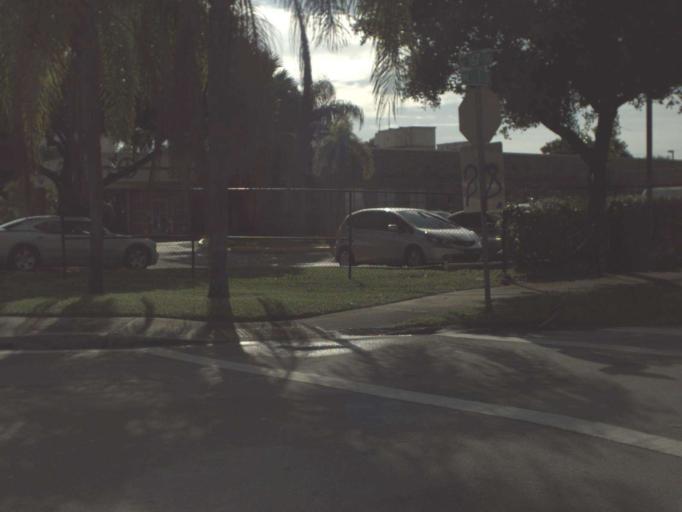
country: US
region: Florida
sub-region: Miami-Dade County
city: Golden Glades
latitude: 25.9281
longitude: -80.1983
